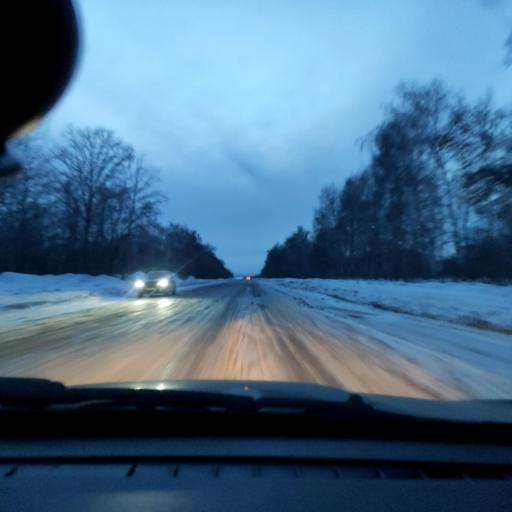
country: RU
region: Samara
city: Tol'yatti
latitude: 53.4960
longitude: 49.2834
